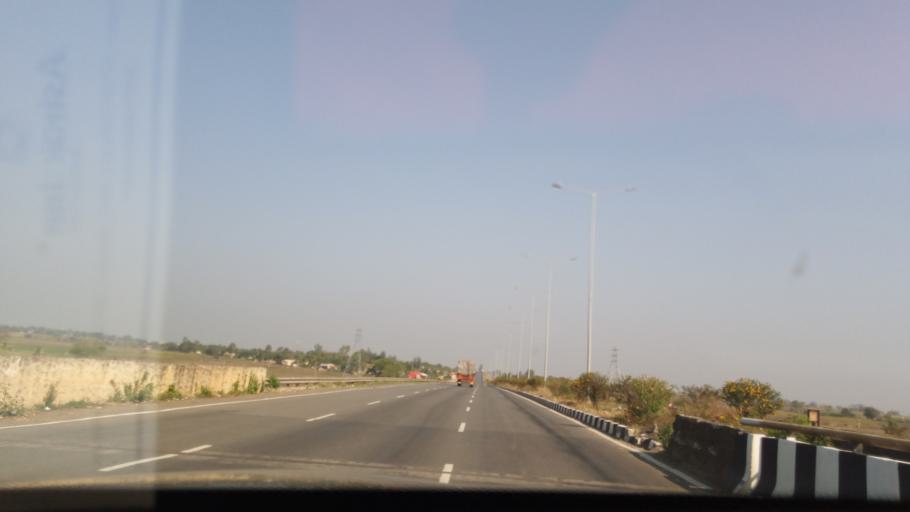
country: IN
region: Karnataka
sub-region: Haveri
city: Haveri
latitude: 14.8639
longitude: 75.3215
